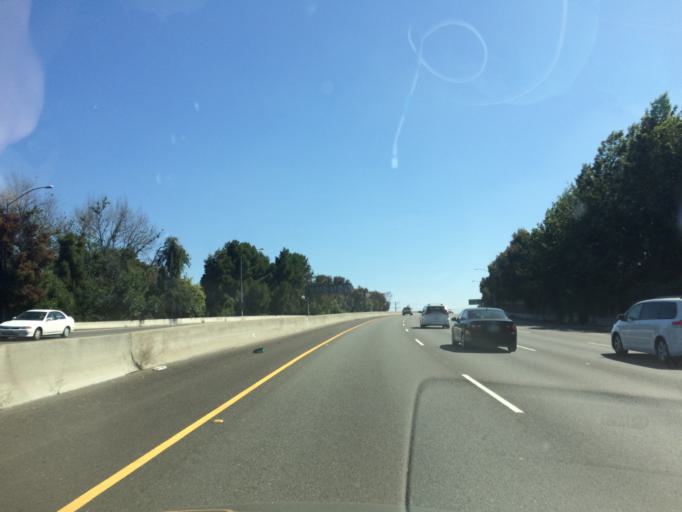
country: US
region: California
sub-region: Santa Clara County
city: Burbank
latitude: 37.3437
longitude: -121.9249
